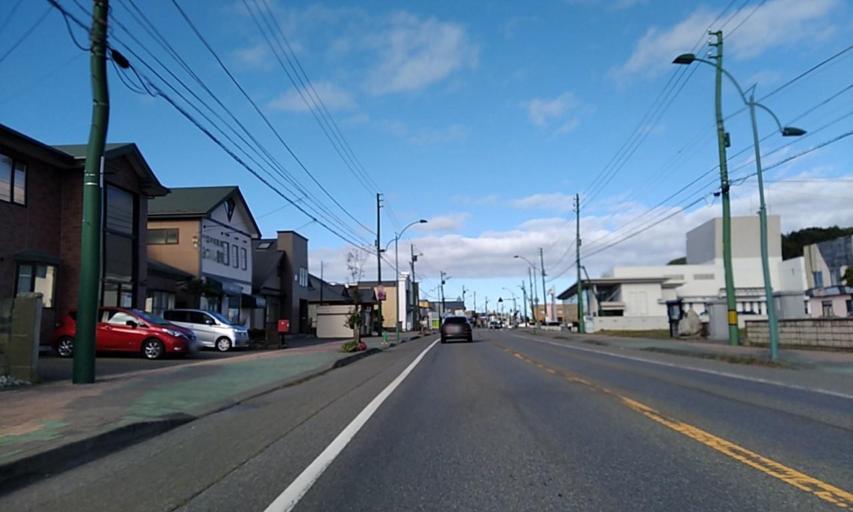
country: JP
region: Hokkaido
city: Shizunai-furukawacho
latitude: 42.2480
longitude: 142.5613
